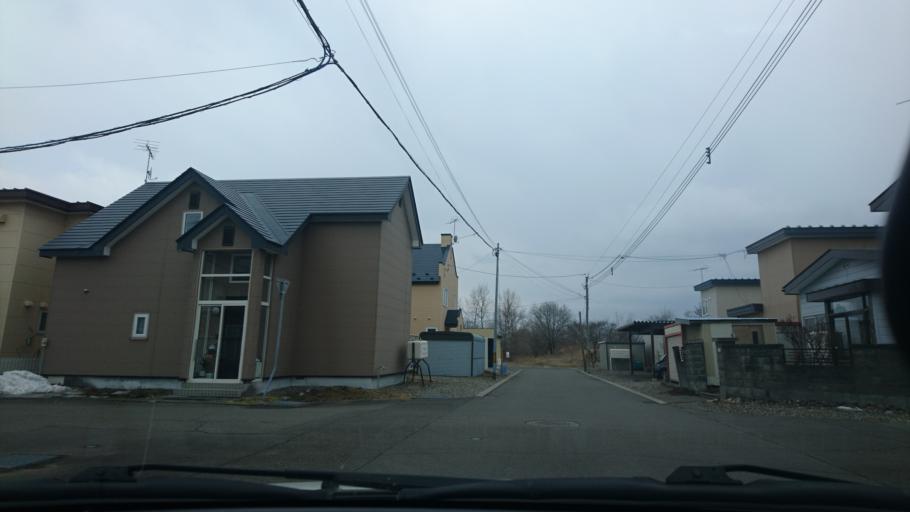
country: JP
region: Hokkaido
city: Otofuke
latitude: 42.9913
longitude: 143.2064
